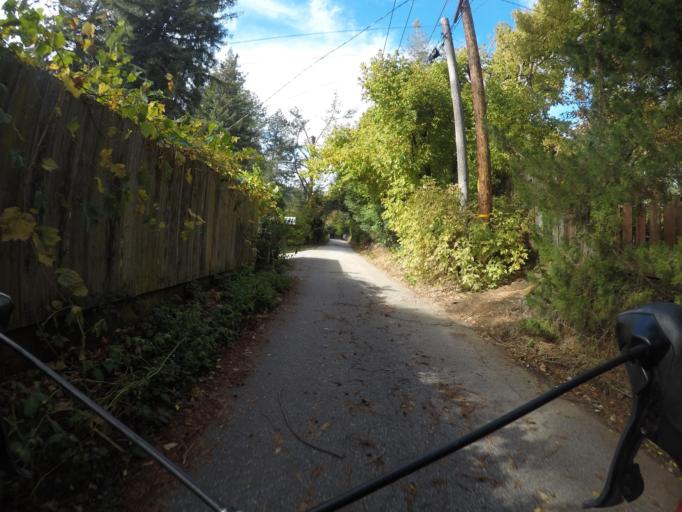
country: US
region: California
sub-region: Santa Cruz County
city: Ben Lomond
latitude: 37.0831
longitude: -122.0798
